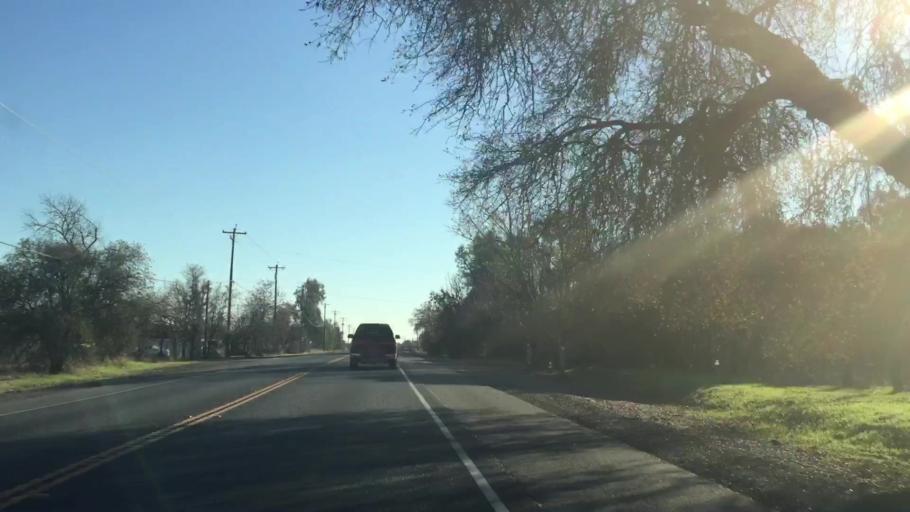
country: US
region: California
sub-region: Butte County
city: Palermo
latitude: 39.4046
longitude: -121.6049
